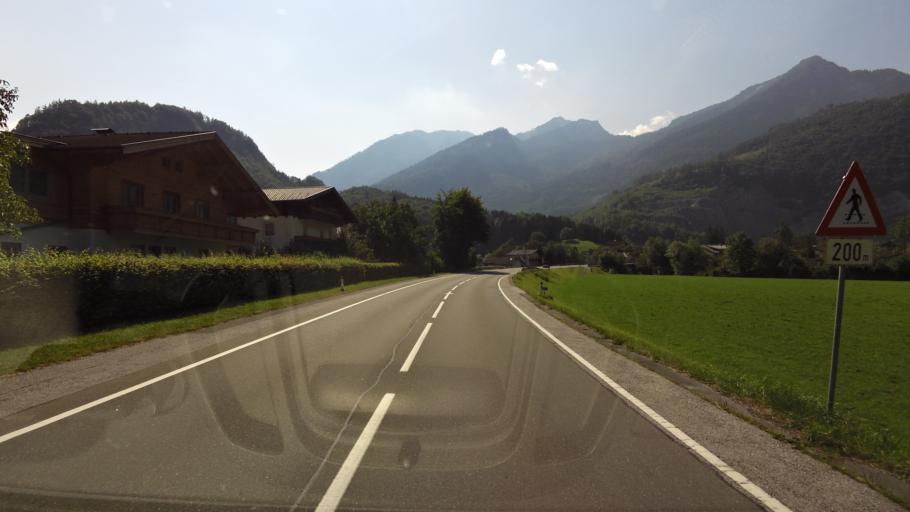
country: AT
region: Salzburg
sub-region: Politischer Bezirk Hallein
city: Golling an der Salzach
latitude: 47.5854
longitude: 13.1811
